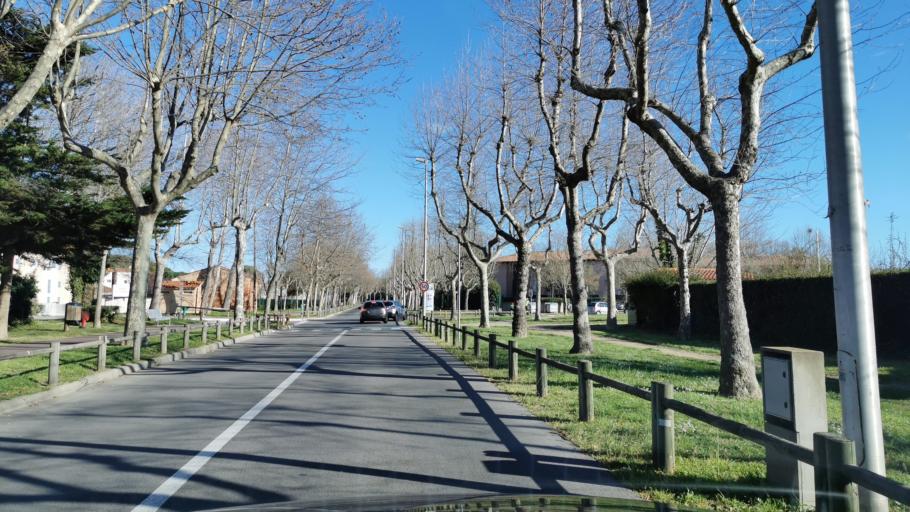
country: FR
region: Languedoc-Roussillon
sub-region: Departement des Pyrenees-Orientales
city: Saint-Cyprien-Plage
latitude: 42.6088
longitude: 3.0309
